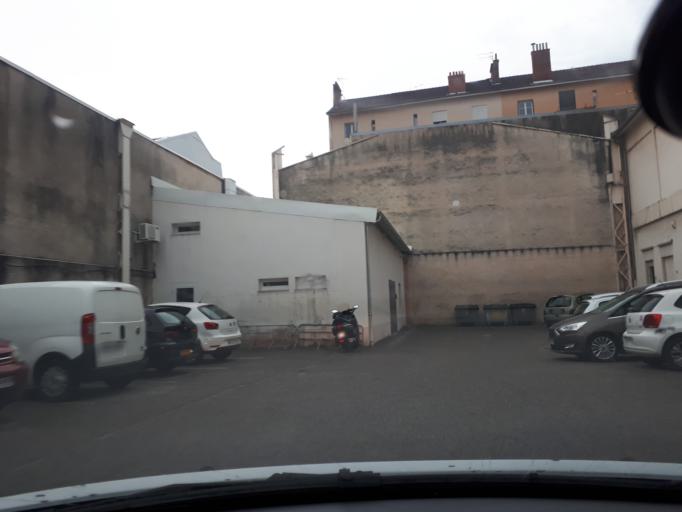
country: FR
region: Rhone-Alpes
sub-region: Departement de l'Isere
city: Saint-Martin-le-Vinoux
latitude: 45.1852
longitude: 5.7113
